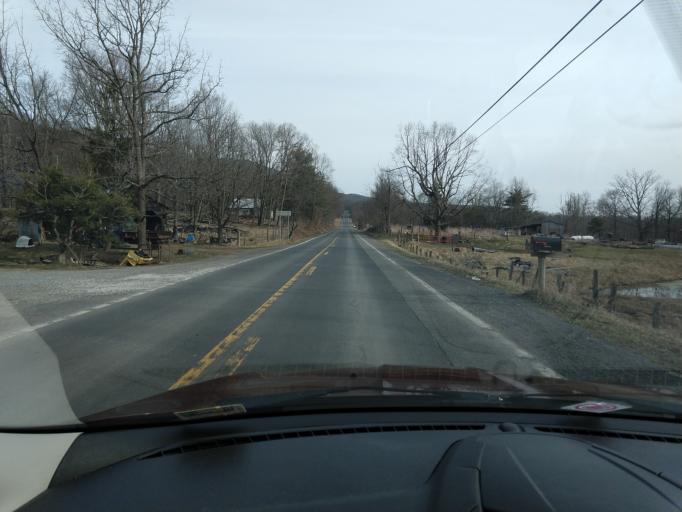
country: US
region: West Virginia
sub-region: Pendleton County
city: Franklin
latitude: 38.6792
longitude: -79.3996
